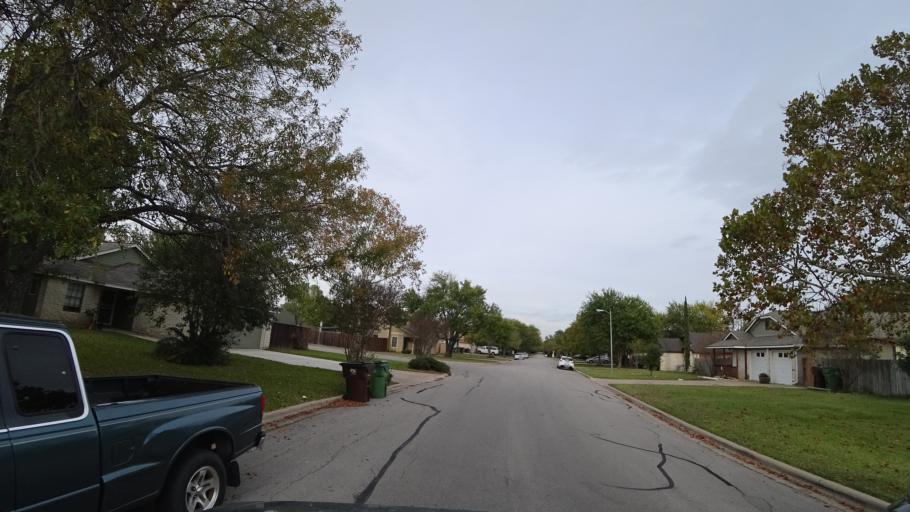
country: US
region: Texas
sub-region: Williamson County
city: Round Rock
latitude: 30.5051
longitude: -97.6660
